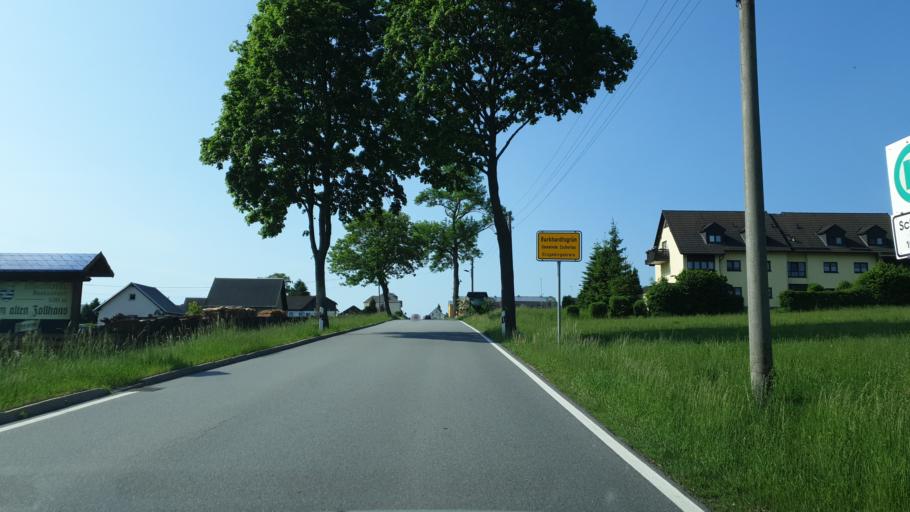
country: DE
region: Saxony
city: Zschorlau
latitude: 50.5417
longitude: 12.6224
